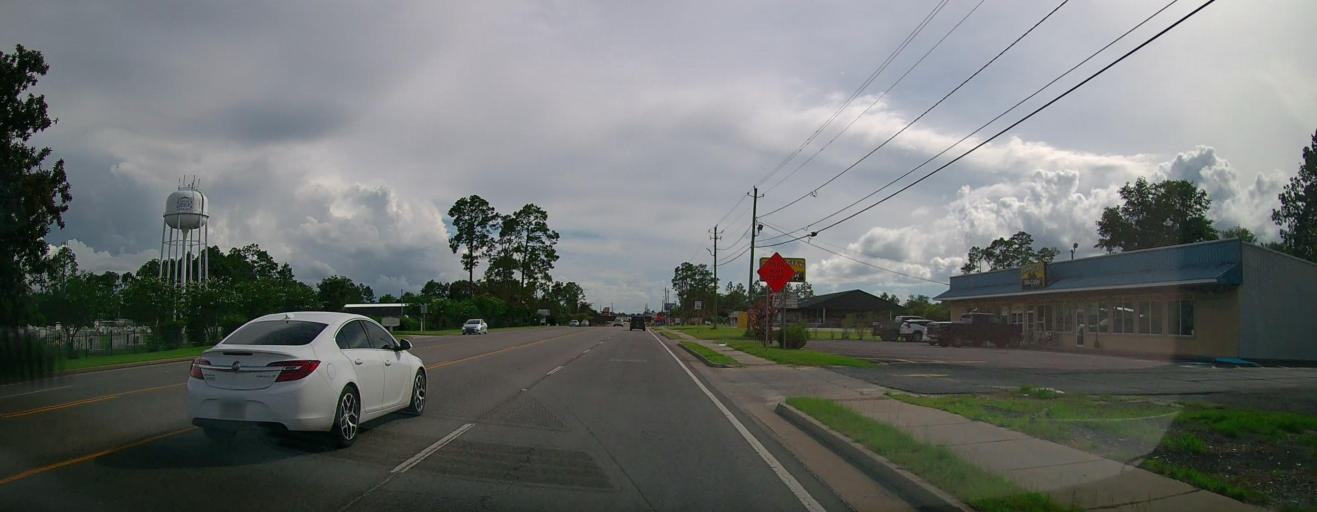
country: US
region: Georgia
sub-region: Wayne County
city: Jesup
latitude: 31.6133
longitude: -81.8786
